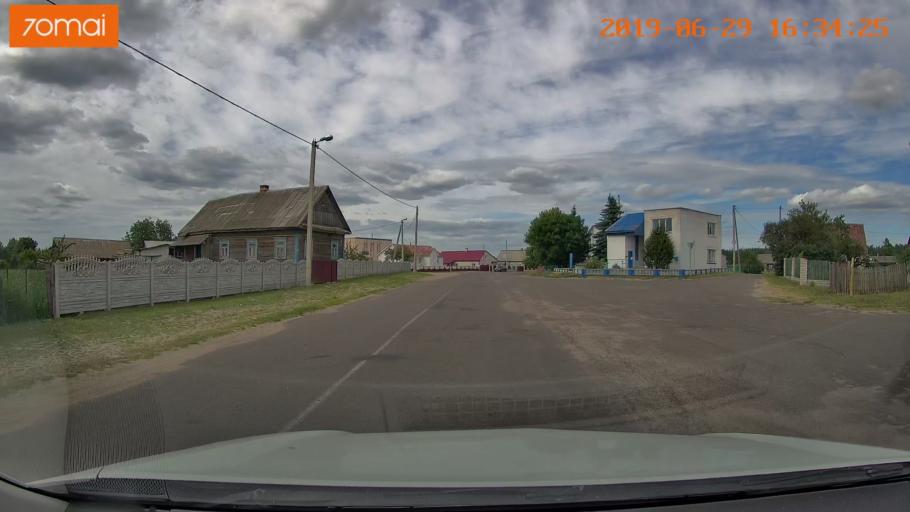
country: BY
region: Brest
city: Luninyets
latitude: 52.2067
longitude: 27.0103
